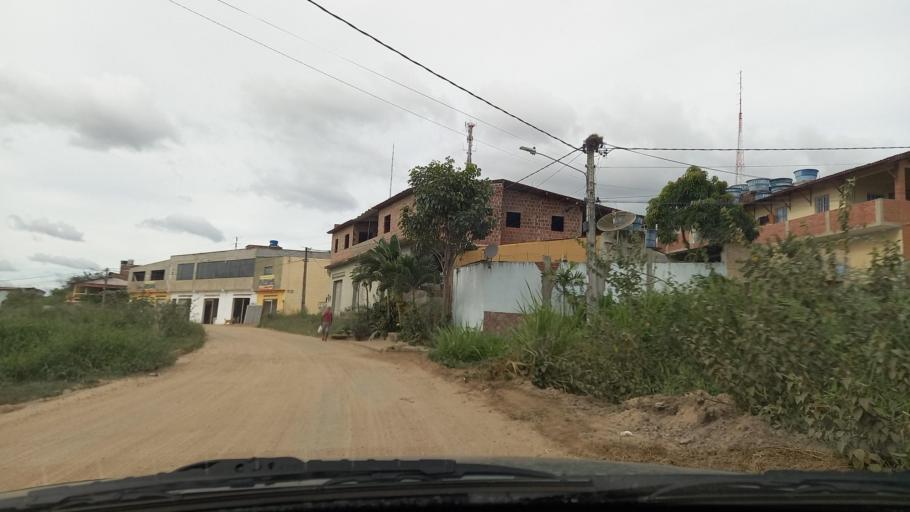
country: BR
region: Pernambuco
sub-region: Gravata
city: Gravata
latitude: -8.2125
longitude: -35.5773
